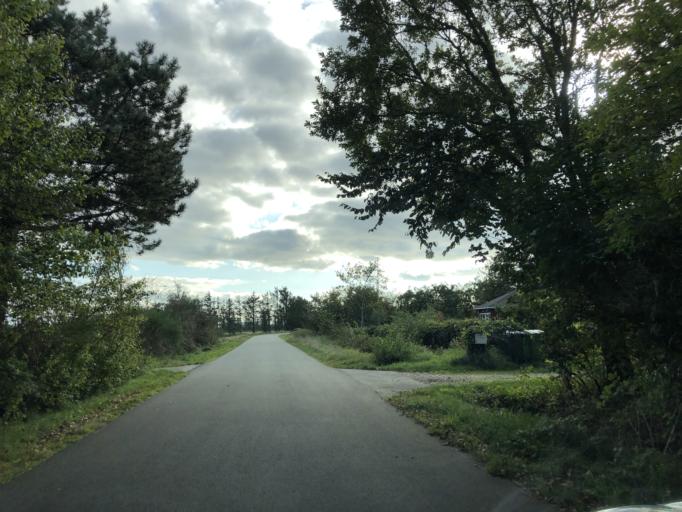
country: DK
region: Central Jutland
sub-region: Holstebro Kommune
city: Ulfborg
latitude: 56.3292
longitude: 8.1593
